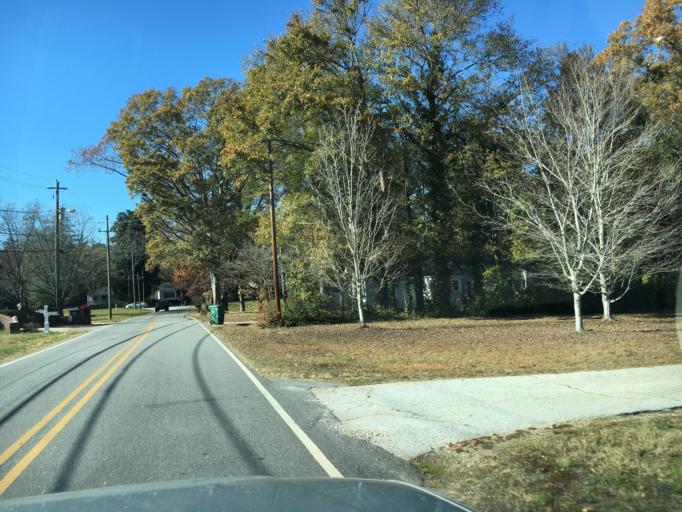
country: US
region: Georgia
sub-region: Hart County
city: Hartwell
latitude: 34.3465
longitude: -82.9411
